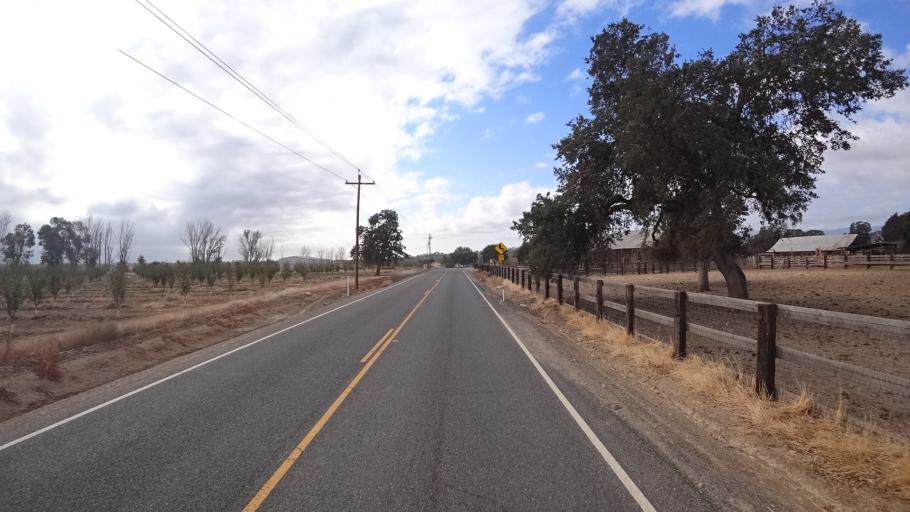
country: US
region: California
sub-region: Yolo County
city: Esparto
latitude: 38.7177
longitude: -122.0471
